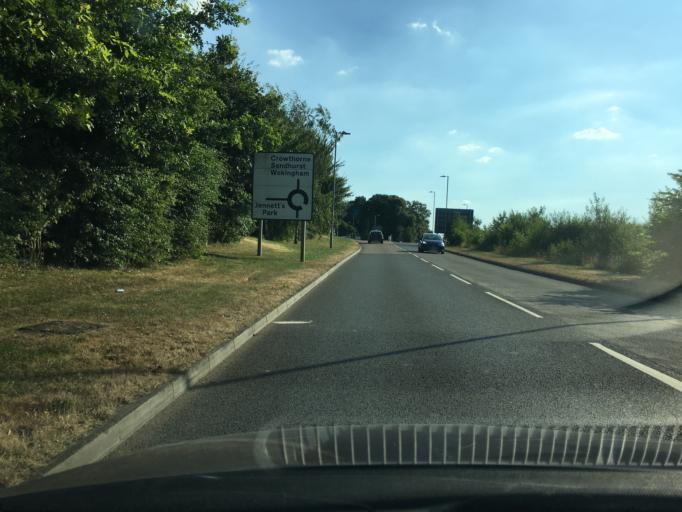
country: GB
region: England
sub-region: Bracknell Forest
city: Binfield
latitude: 51.4086
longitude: -0.7855
